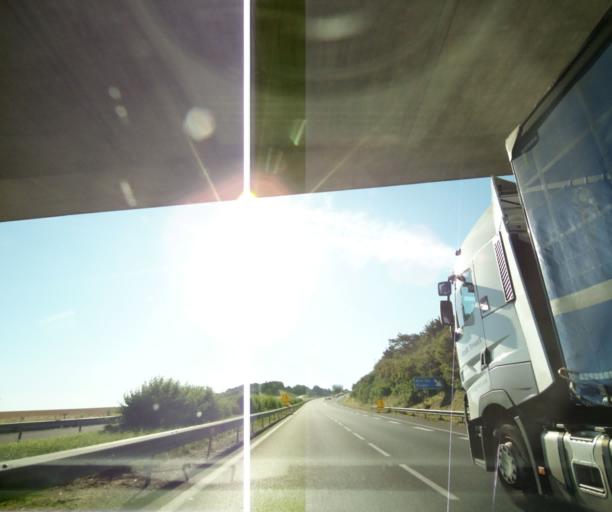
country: FR
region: Bourgogne
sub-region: Departement de l'Yonne
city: Vinneuf
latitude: 48.3715
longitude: 3.1178
